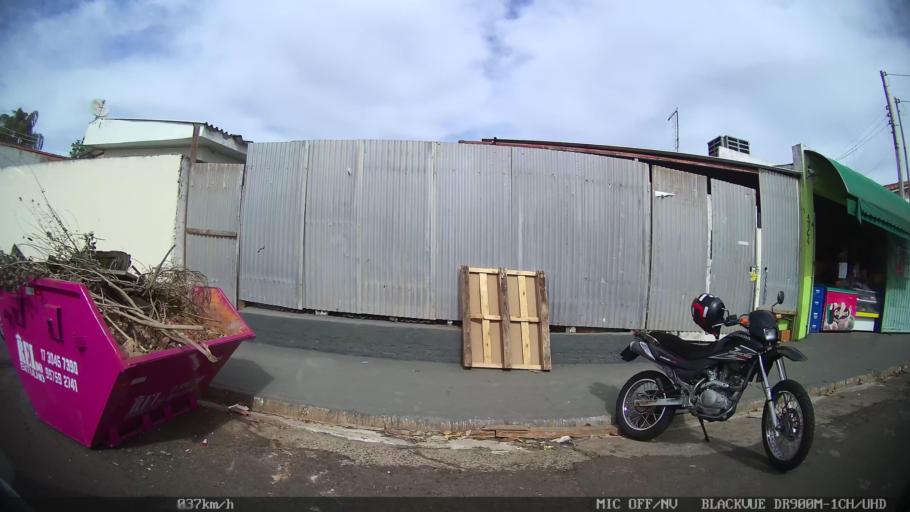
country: BR
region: Sao Paulo
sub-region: Catanduva
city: Catanduva
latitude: -21.1509
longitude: -48.9645
